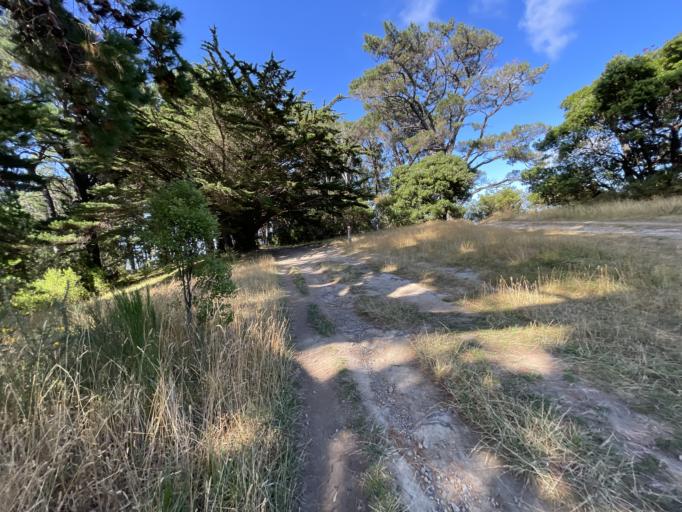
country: NZ
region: Wellington
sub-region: Wellington City
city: Wellington
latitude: -41.3072
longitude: 174.7882
